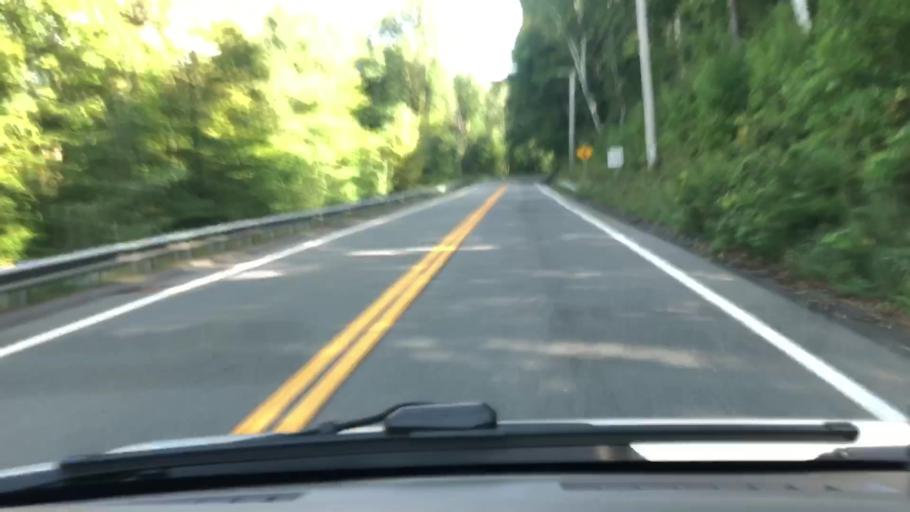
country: US
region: Massachusetts
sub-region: Berkshire County
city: North Adams
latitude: 42.7037
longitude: -73.0682
